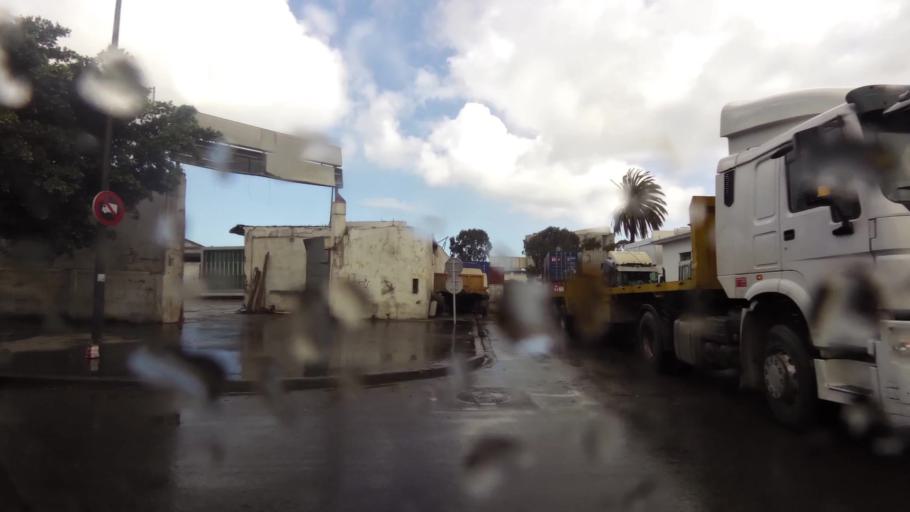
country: MA
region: Grand Casablanca
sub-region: Casablanca
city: Casablanca
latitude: 33.5962
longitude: -7.5991
